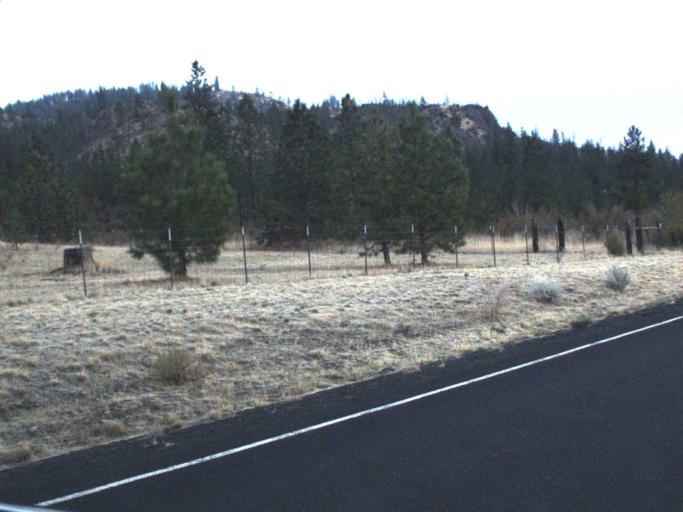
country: US
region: Washington
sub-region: Lincoln County
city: Davenport
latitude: 47.9045
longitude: -118.2749
